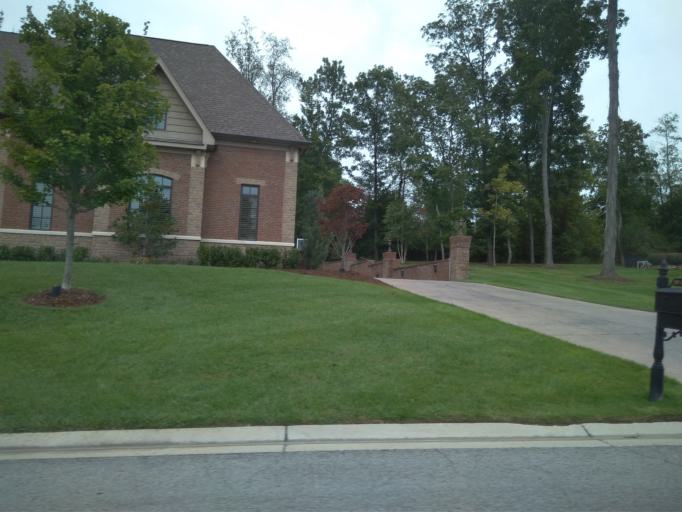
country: US
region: Kentucky
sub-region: Oldham County
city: Pewee Valley
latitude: 38.2789
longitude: -85.4734
